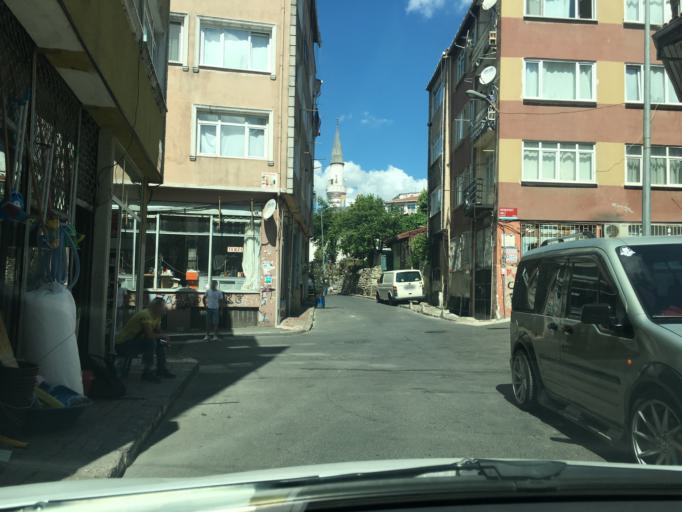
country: TR
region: Istanbul
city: Istanbul
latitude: 41.0119
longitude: 28.9261
